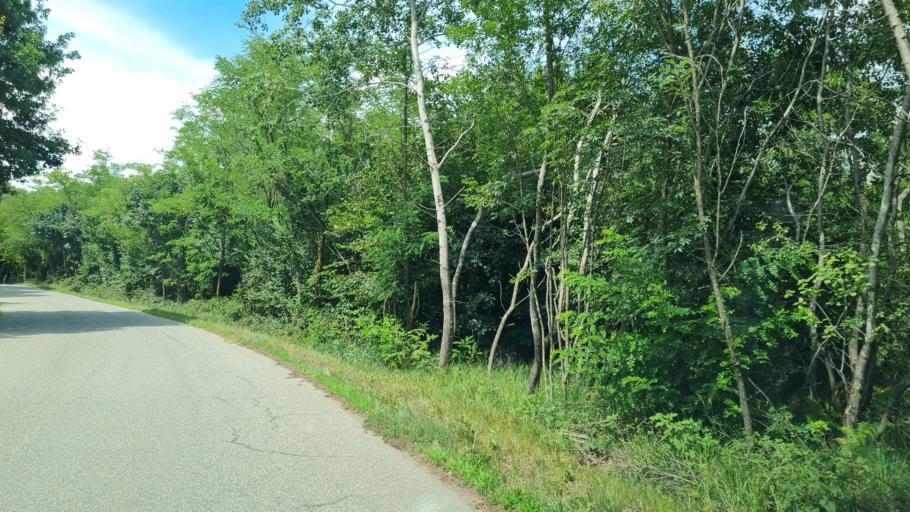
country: IT
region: Piedmont
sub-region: Provincia di Biella
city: Castelletto Cervo
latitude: 45.5480
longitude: 8.2264
